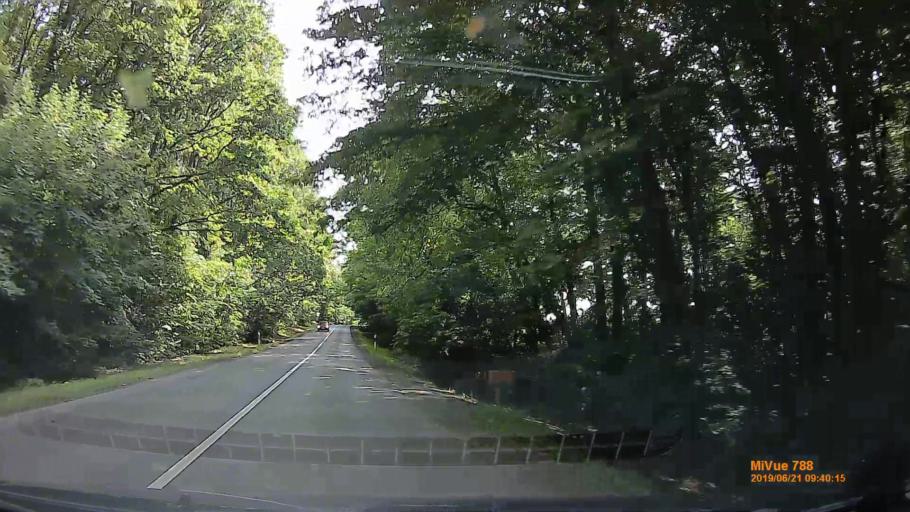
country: HU
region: Somogy
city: Taszar
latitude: 46.2934
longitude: 17.9403
